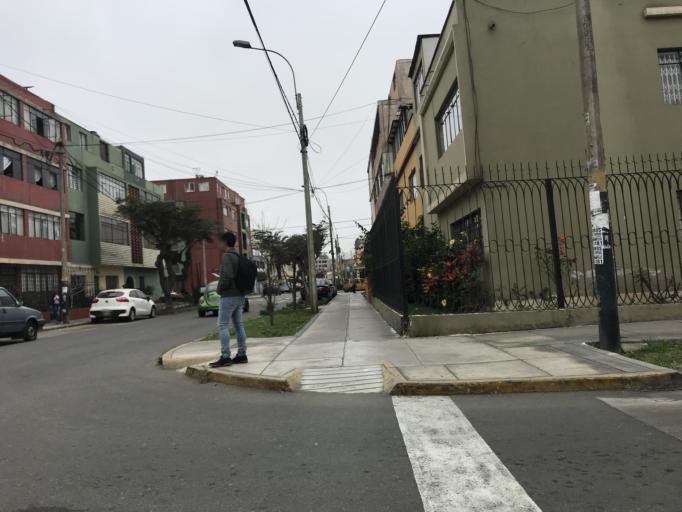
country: PE
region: Lima
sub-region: Lima
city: San Isidro
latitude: -12.0834
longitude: -77.0627
